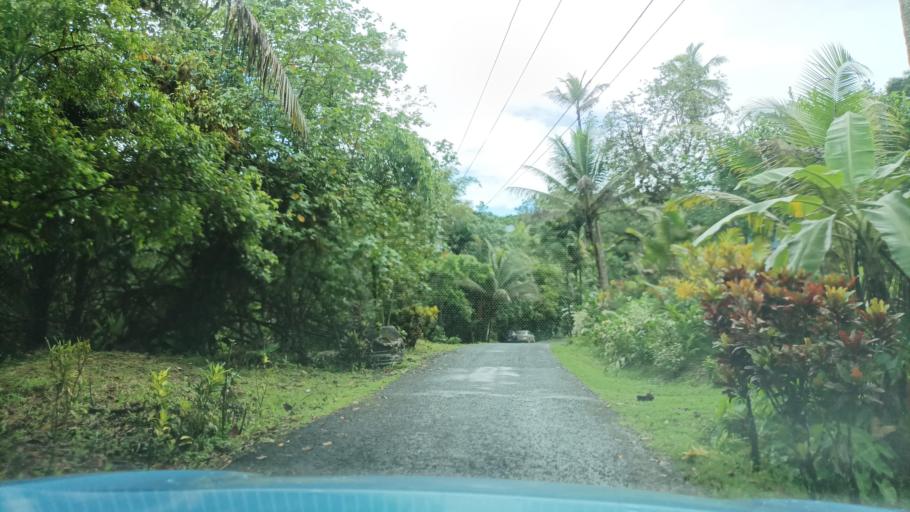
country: FM
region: Pohnpei
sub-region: Sokehs Municipality
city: Palikir - National Government Center
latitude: 6.8258
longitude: 158.1693
